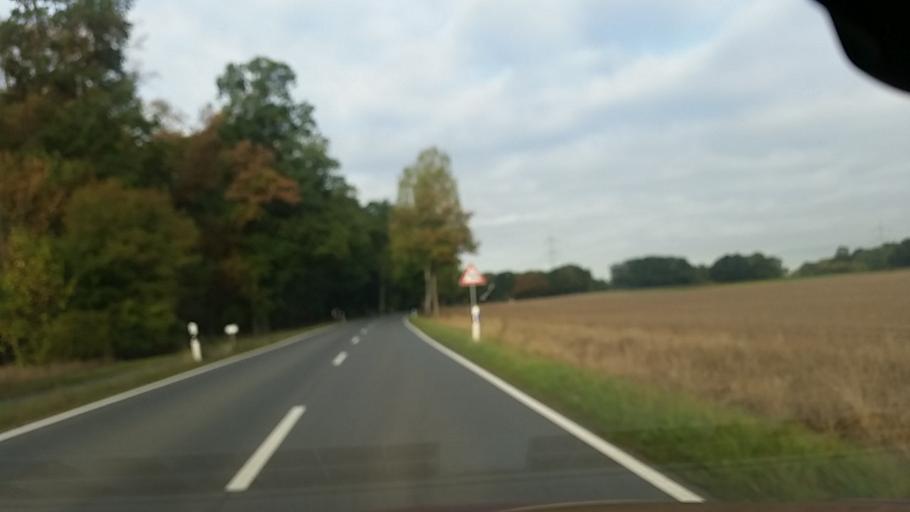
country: DE
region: Lower Saxony
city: Ahnsbeck
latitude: 52.5941
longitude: 10.3183
